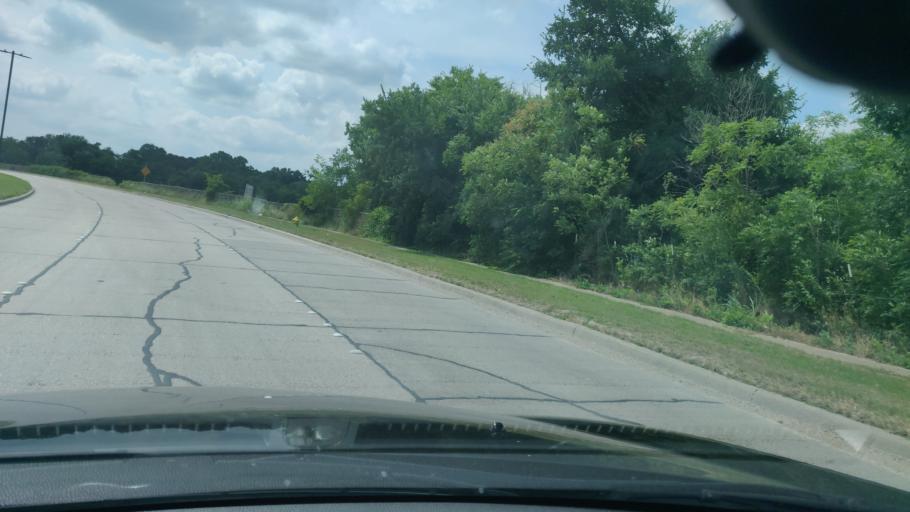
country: US
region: Texas
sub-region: Dallas County
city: Rowlett
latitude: 32.9309
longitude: -96.5889
